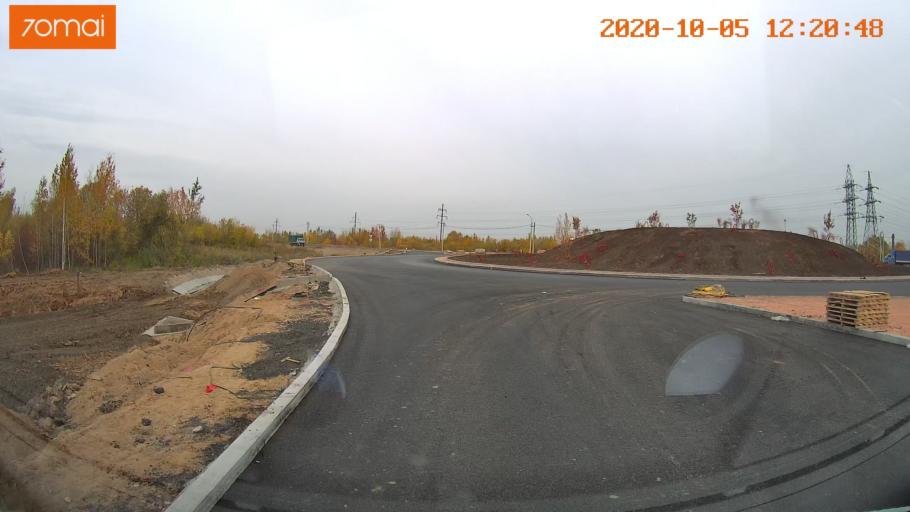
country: RU
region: Ivanovo
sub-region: Gorod Ivanovo
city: Ivanovo
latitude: 56.9663
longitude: 40.9318
